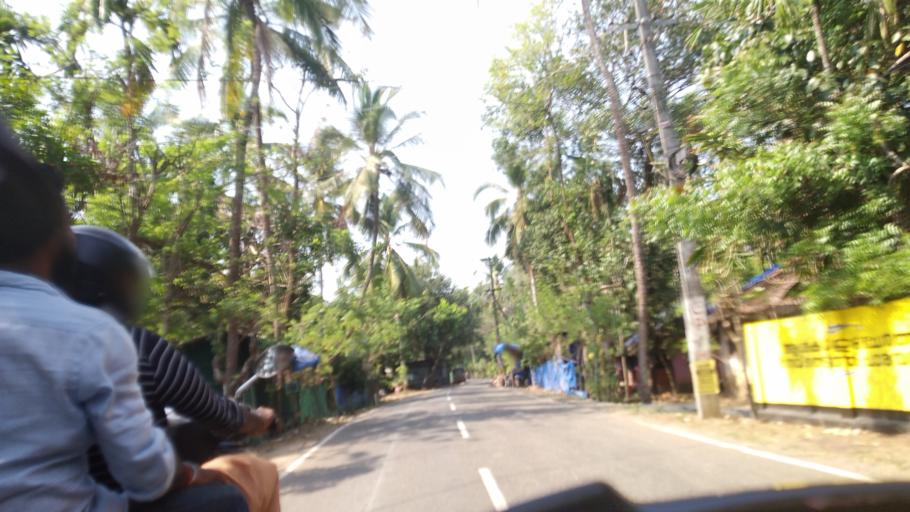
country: IN
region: Kerala
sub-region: Thrissur District
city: Thanniyam
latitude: 10.3837
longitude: 76.0998
